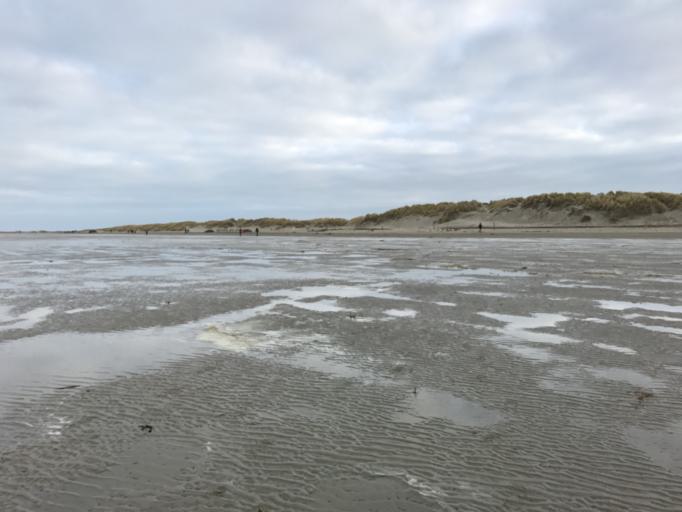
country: DE
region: Lower Saxony
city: Borkum
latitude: 53.5939
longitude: 6.6564
